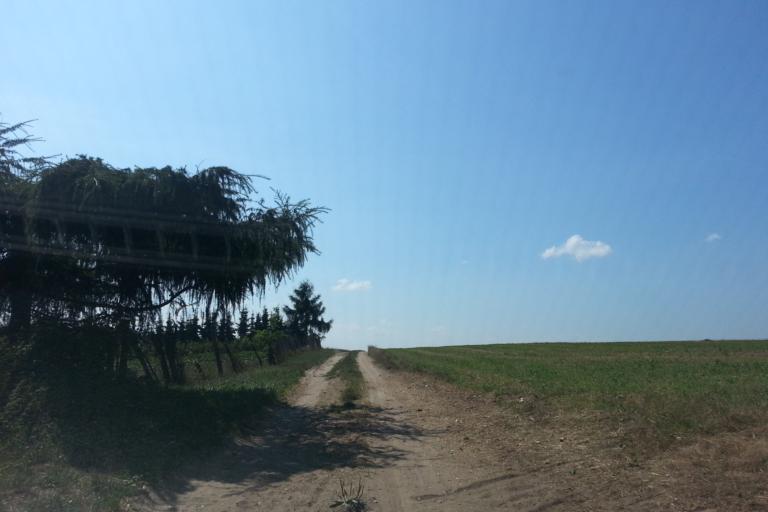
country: DE
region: Mecklenburg-Vorpommern
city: Ducherow
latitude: 53.7005
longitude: 13.8020
